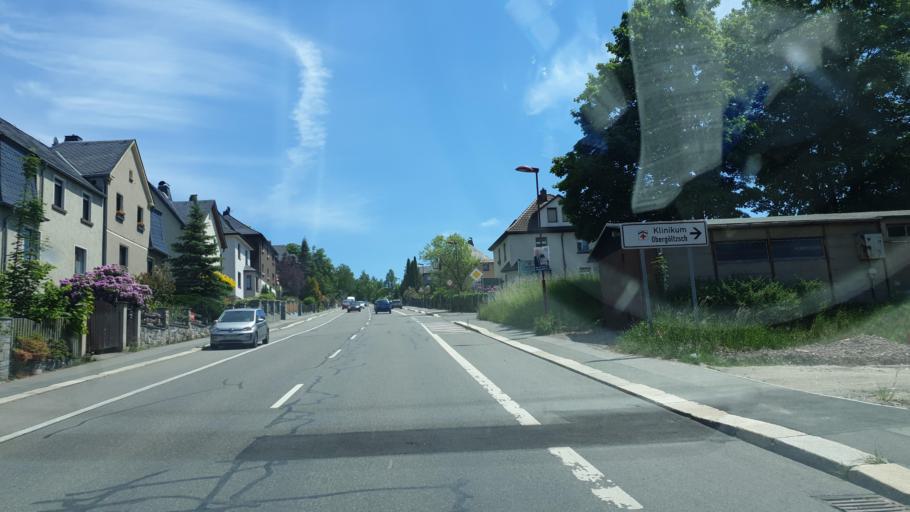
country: DE
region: Saxony
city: Rodewisch
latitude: 50.5270
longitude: 12.4120
